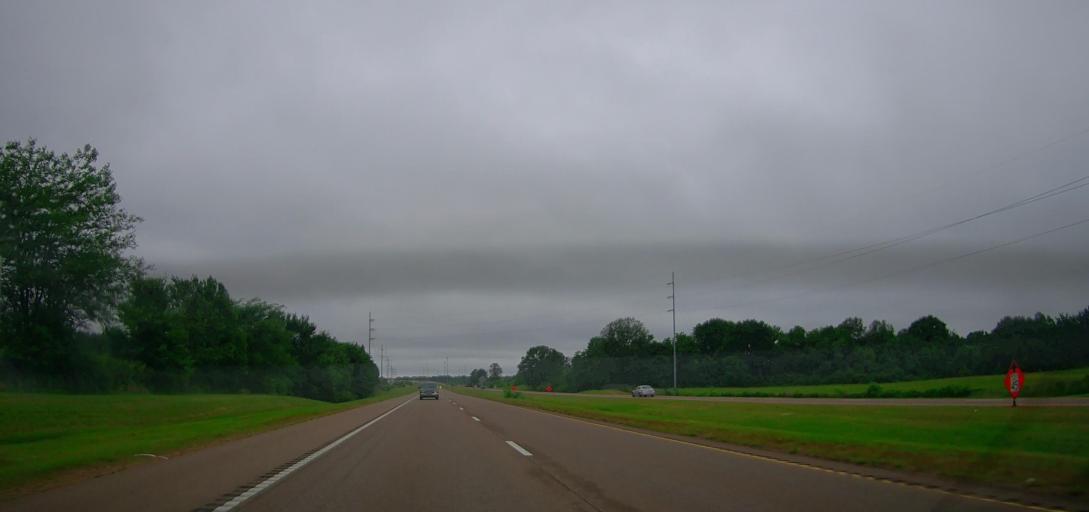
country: US
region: Mississippi
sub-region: De Soto County
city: Olive Branch
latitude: 34.9691
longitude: -89.8150
